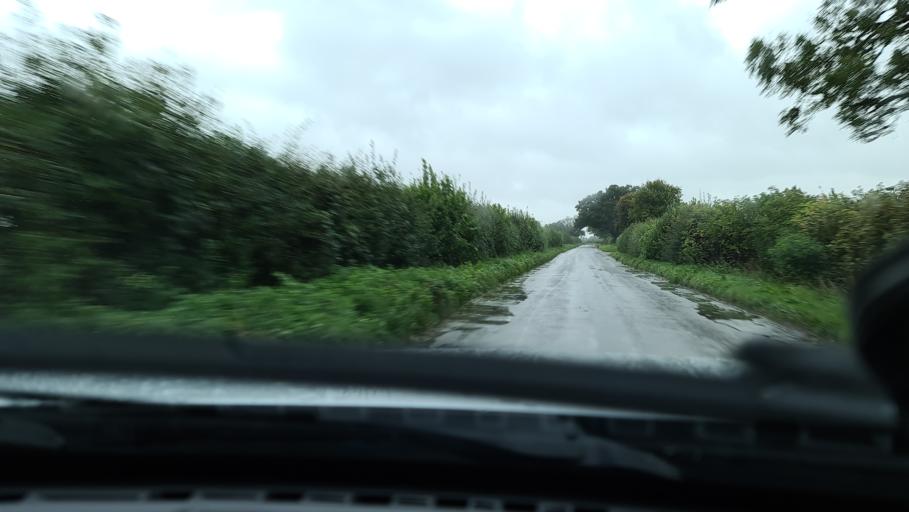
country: GB
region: England
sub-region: Oxfordshire
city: Woodstock
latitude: 51.8983
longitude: -1.3829
